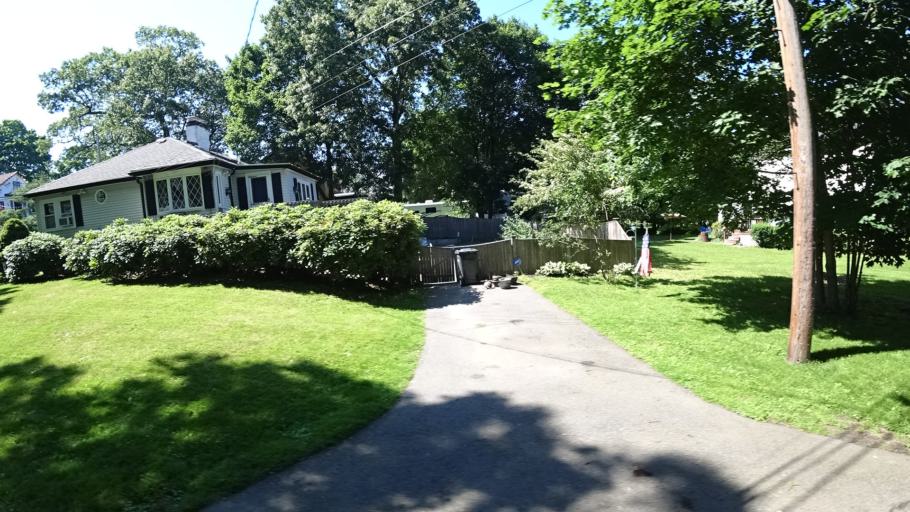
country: US
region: Massachusetts
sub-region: Norfolk County
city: Dedham
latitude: 42.2401
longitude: -71.1528
